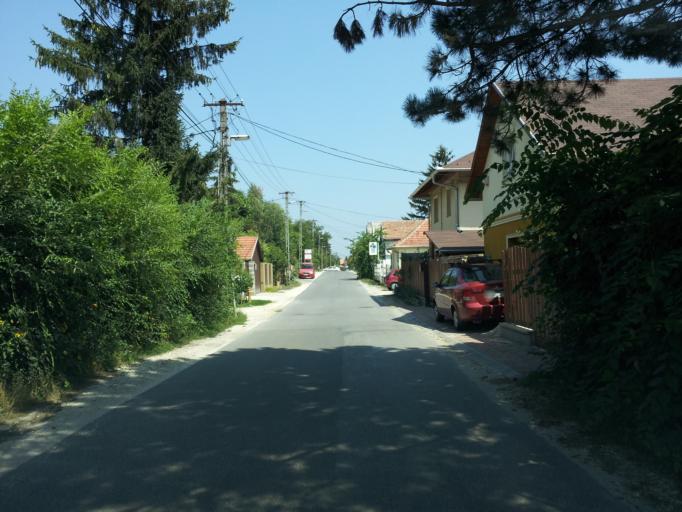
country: HU
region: Pest
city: Szigetszentmiklos
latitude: 47.3245
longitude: 19.0422
